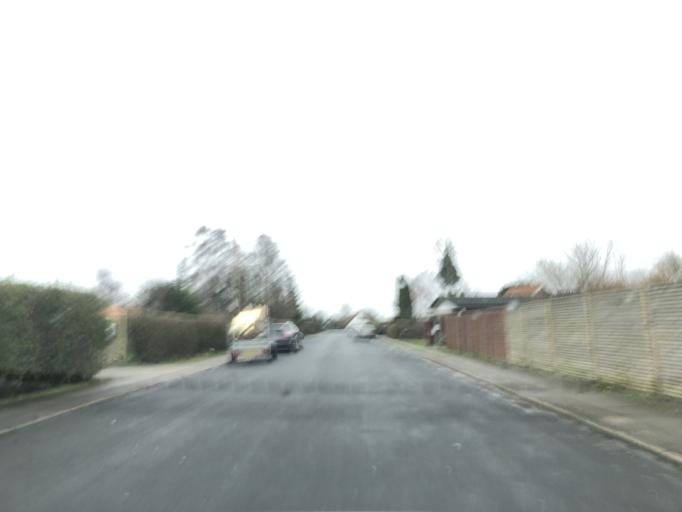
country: DK
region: Capital Region
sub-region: Dragor Kommune
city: Dragor
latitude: 55.5856
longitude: 12.6420
